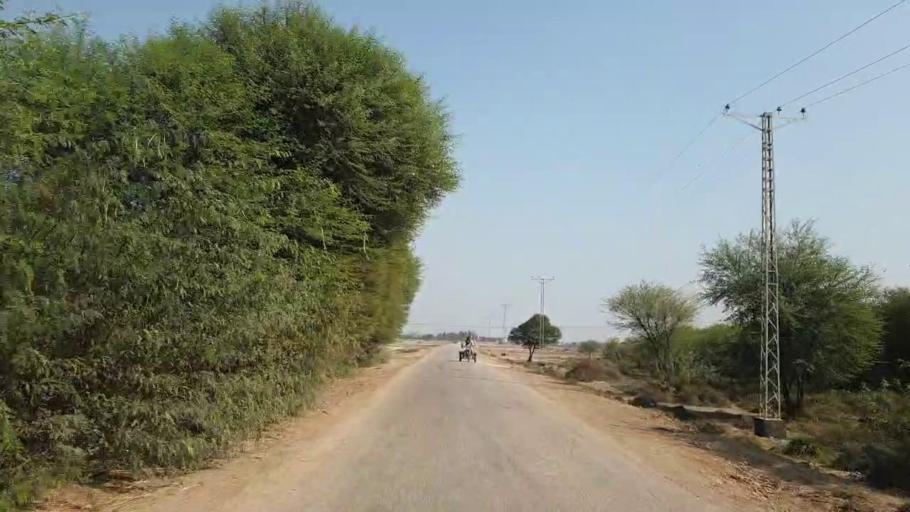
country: PK
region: Sindh
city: Matiari
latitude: 25.5018
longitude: 68.4487
